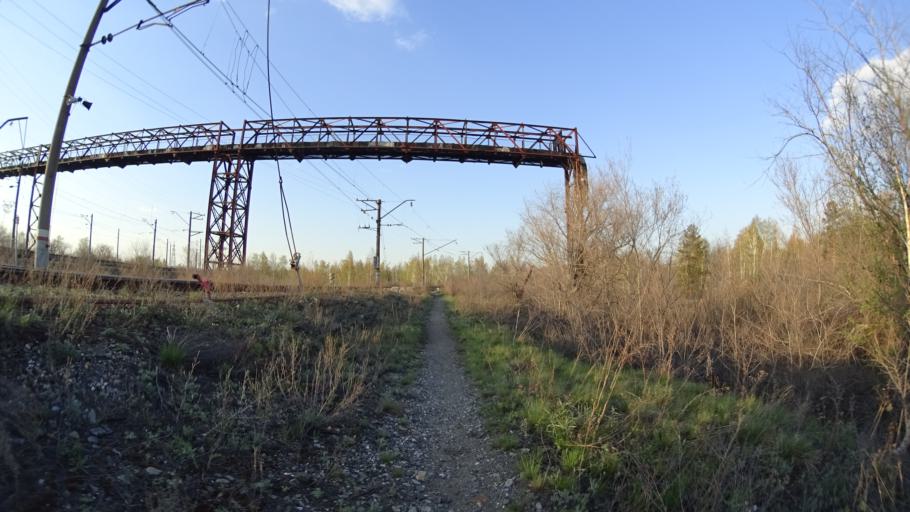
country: RU
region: Chelyabinsk
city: Troitsk
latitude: 54.0576
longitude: 61.6140
